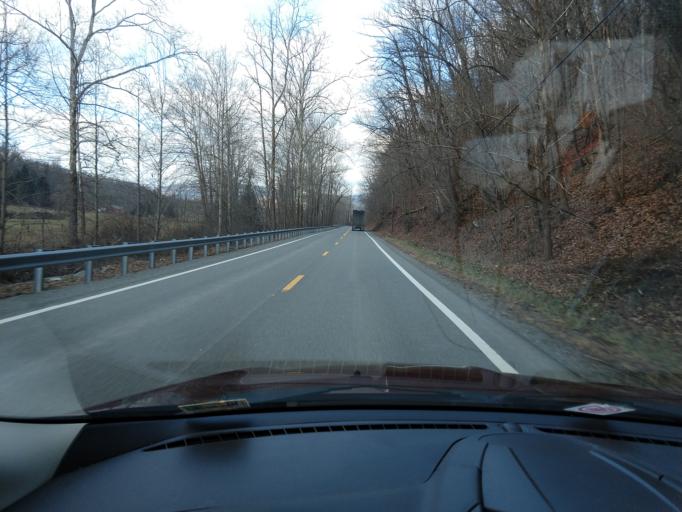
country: US
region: West Virginia
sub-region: Randolph County
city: Elkins
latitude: 38.6765
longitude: -79.9563
